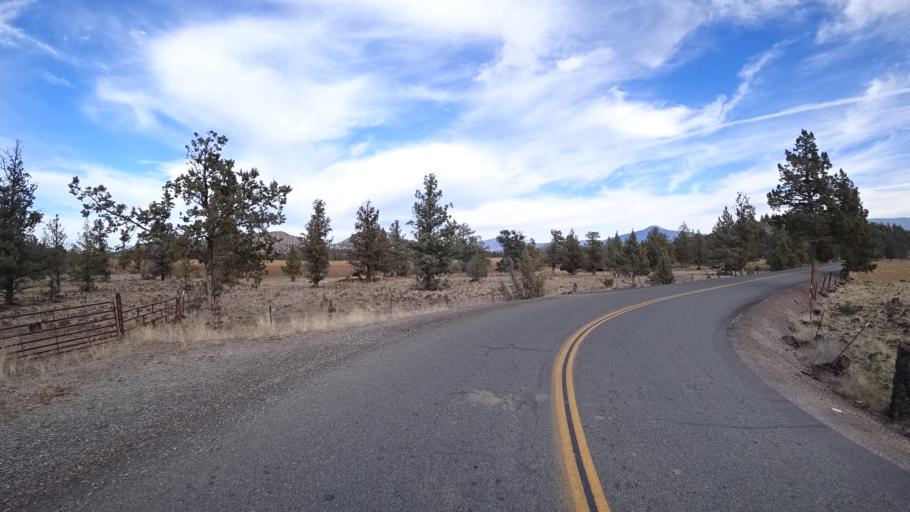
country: US
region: California
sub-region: Siskiyou County
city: Montague
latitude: 41.6385
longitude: -122.4380
